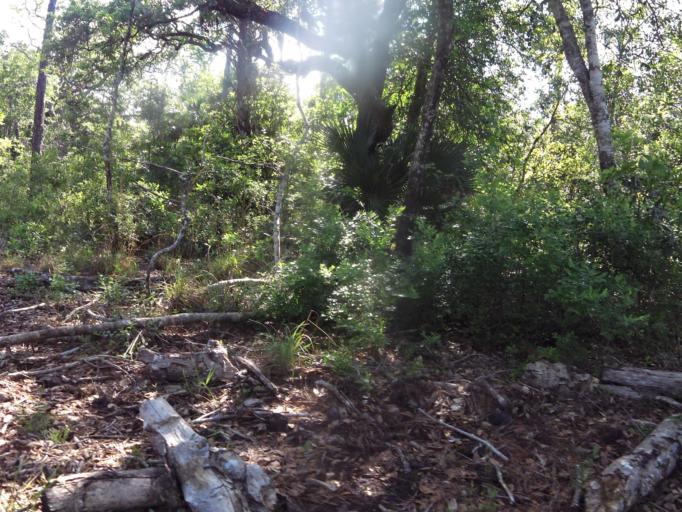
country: US
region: Florida
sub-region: Saint Johns County
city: Palm Valley
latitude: 30.1330
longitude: -81.3723
